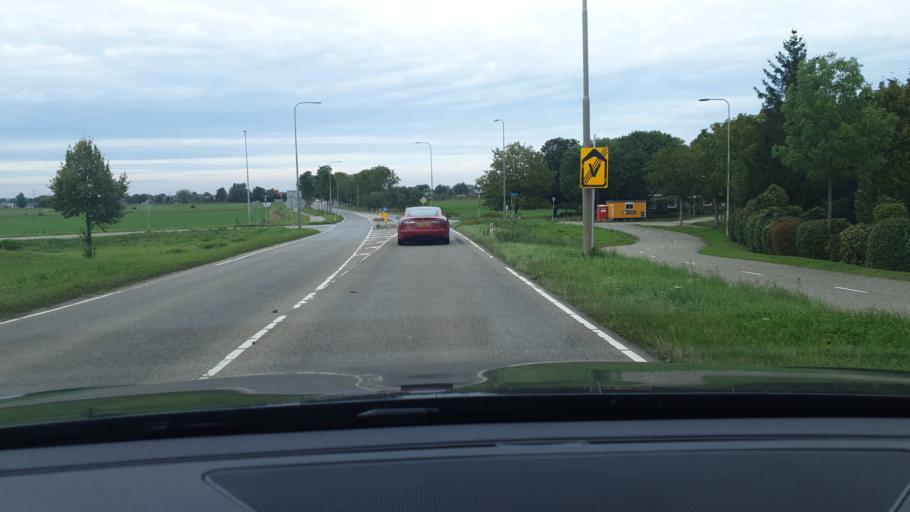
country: NL
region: Gelderland
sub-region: Gemeente Overbetuwe
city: Oosterhout
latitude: 51.8977
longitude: 5.8368
